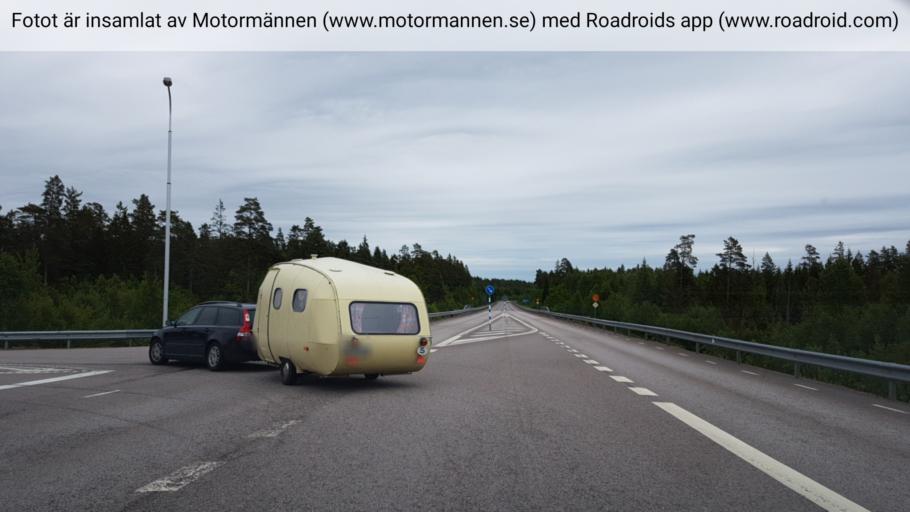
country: SE
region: Kalmar
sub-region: Oskarshamns Kommun
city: Oskarshamn
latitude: 57.3734
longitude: 16.4914
